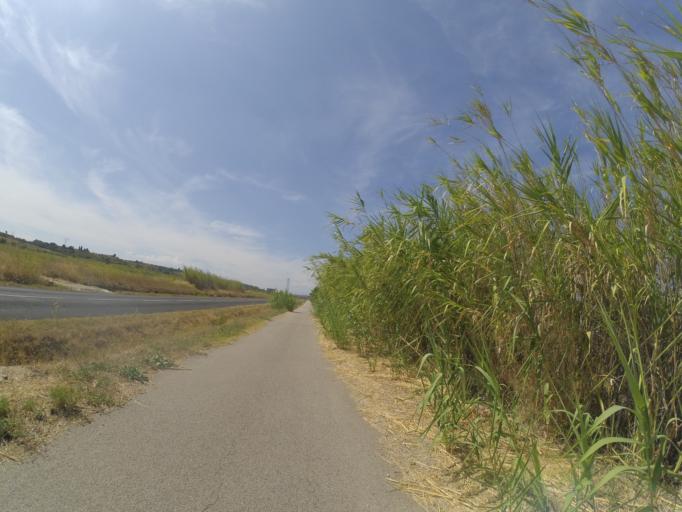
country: FR
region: Languedoc-Roussillon
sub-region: Departement des Pyrenees-Orientales
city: Peyrestortes
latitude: 42.7566
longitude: 2.8329
